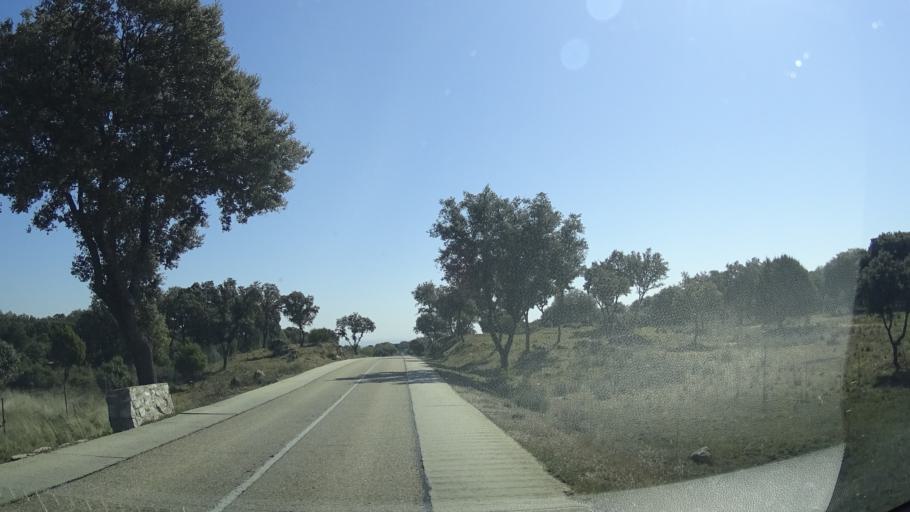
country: ES
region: Madrid
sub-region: Provincia de Madrid
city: Colmenar Viejo
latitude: 40.6447
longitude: -3.8376
